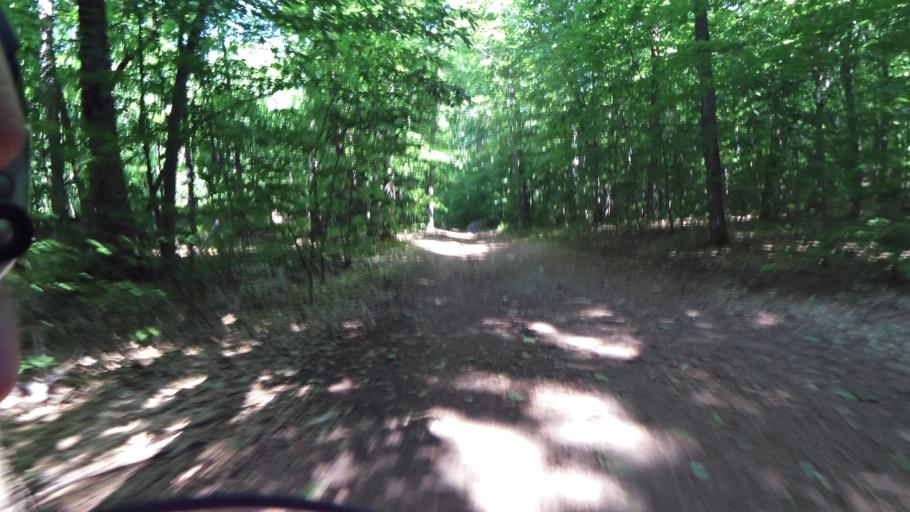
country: CA
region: Quebec
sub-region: Outaouais
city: Wakefield
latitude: 45.5318
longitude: -75.8655
